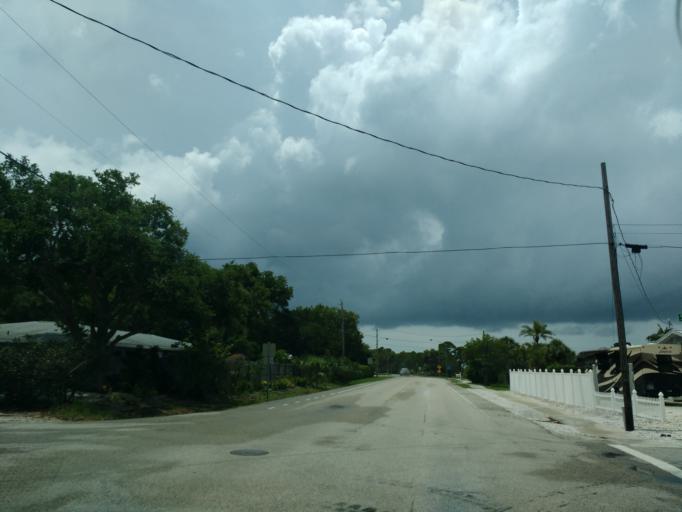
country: US
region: Florida
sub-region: Sarasota County
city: Venice
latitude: 27.0802
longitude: -82.4503
